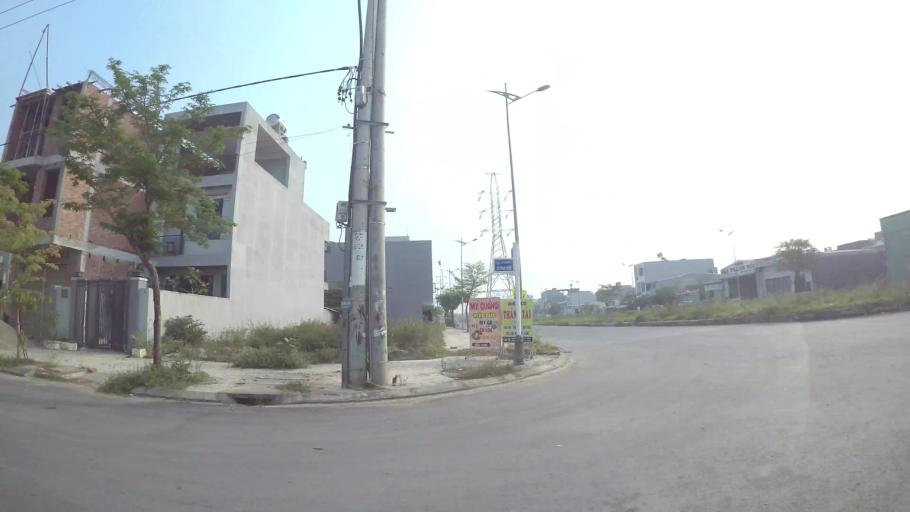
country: VN
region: Da Nang
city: Cam Le
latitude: 16.0094
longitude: 108.2213
